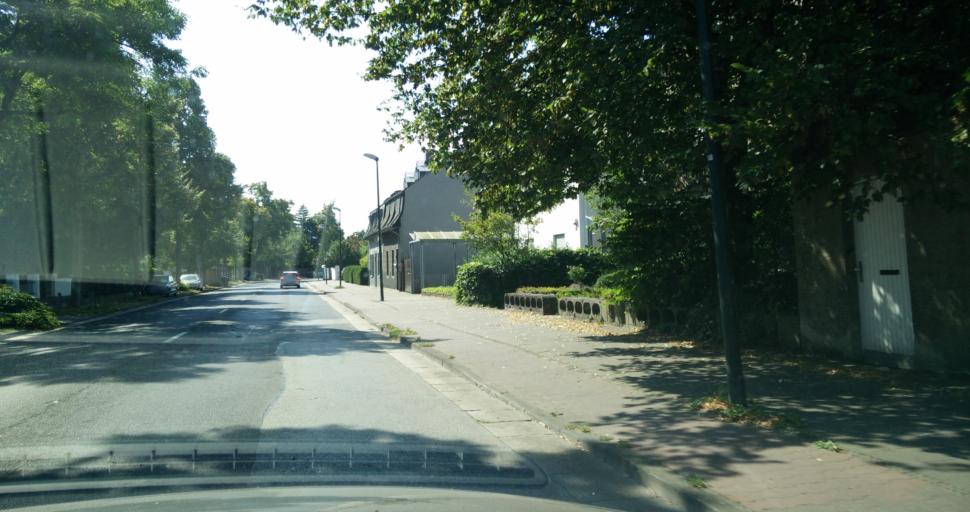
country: DE
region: North Rhine-Westphalia
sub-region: Regierungsbezirk Dusseldorf
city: Meerbusch
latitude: 51.3093
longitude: 6.7433
